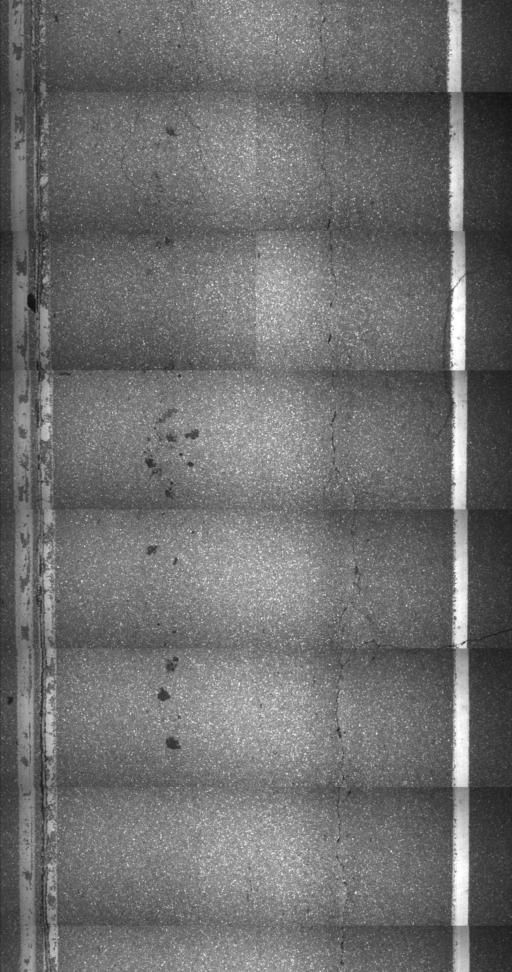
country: US
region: Vermont
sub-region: Caledonia County
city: Hardwick
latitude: 44.4219
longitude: -72.4111
